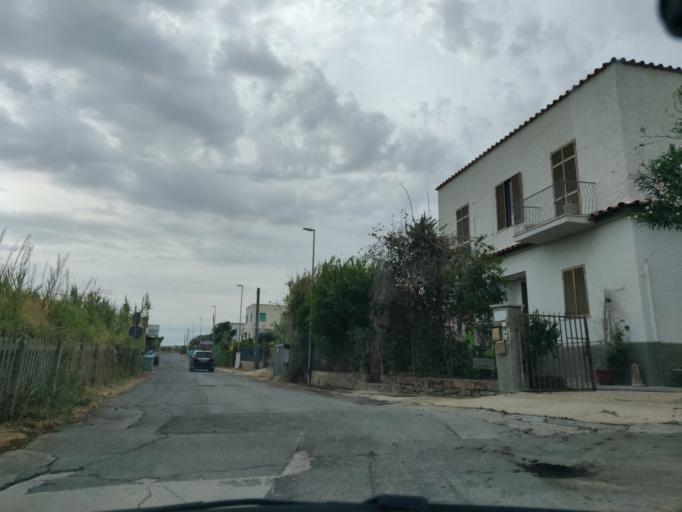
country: IT
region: Latium
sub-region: Citta metropolitana di Roma Capitale
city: Santa Marinella
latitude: 42.0408
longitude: 11.9125
